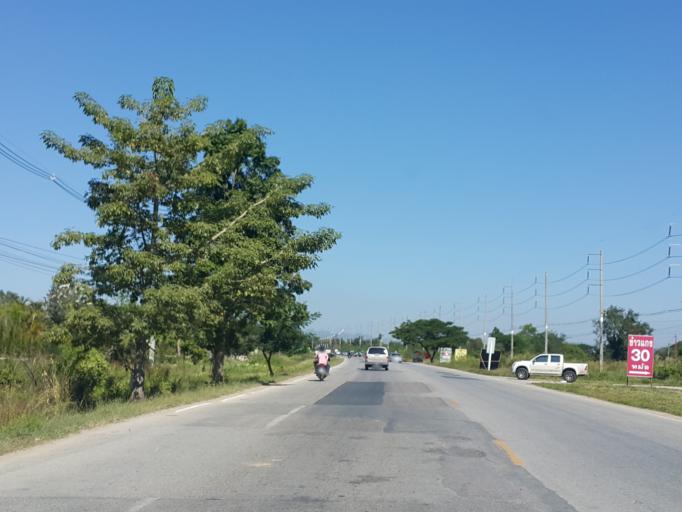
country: TH
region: Chiang Mai
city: San Kamphaeng
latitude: 18.7781
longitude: 99.0696
